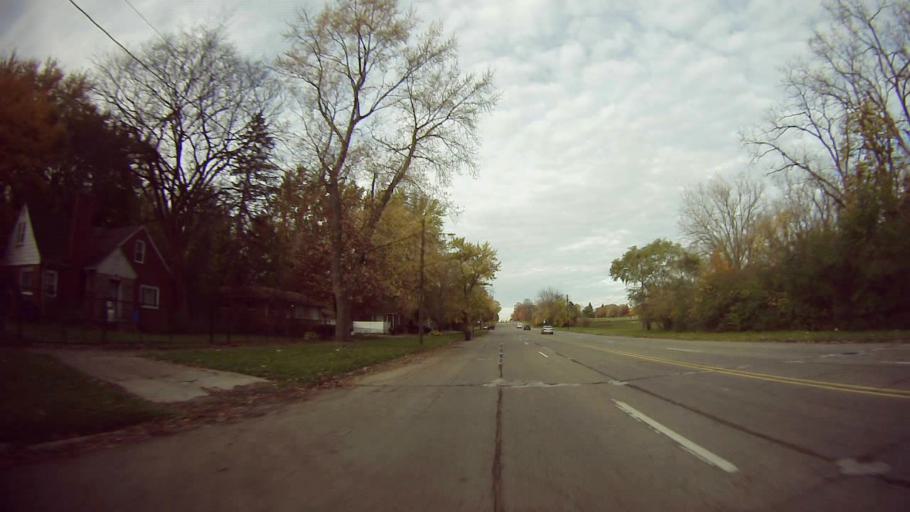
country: US
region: Michigan
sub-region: Wayne County
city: Redford
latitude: 42.4147
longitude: -83.2680
